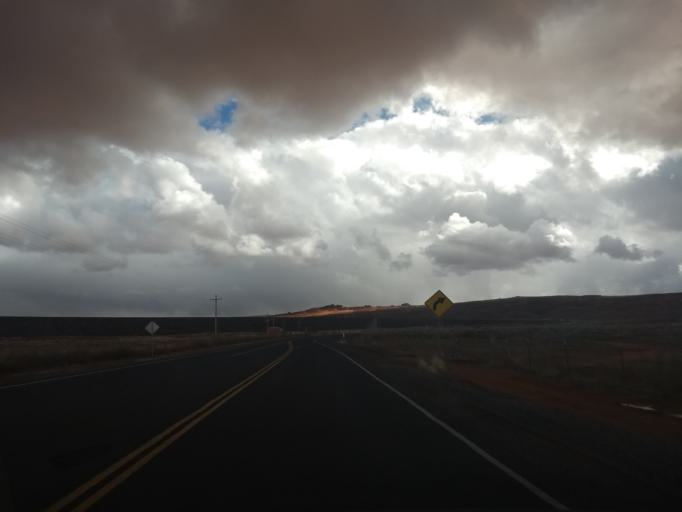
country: US
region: Utah
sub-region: Washington County
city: Hurricane
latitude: 37.1172
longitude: -113.3914
